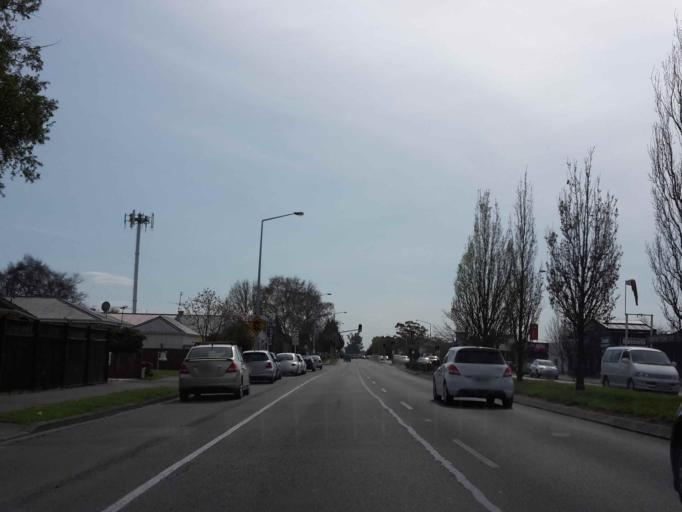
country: NZ
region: Canterbury
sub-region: Waimakariri District
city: Kaiapoi
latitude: -43.4462
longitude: 172.6316
